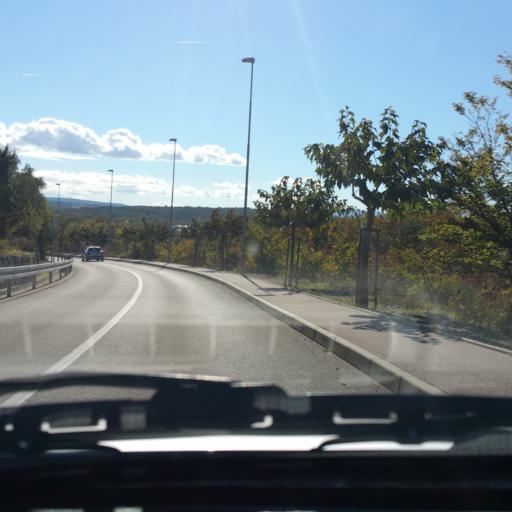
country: HR
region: Primorsko-Goranska
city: Omisalj
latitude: 45.2043
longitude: 14.5605
